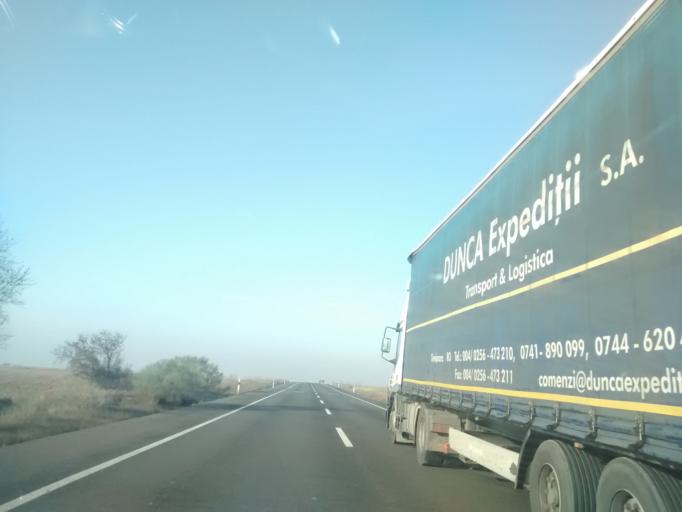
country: ES
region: Aragon
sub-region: Provincia de Huesca
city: Saidi / Zaidin
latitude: 41.5157
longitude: 0.2561
